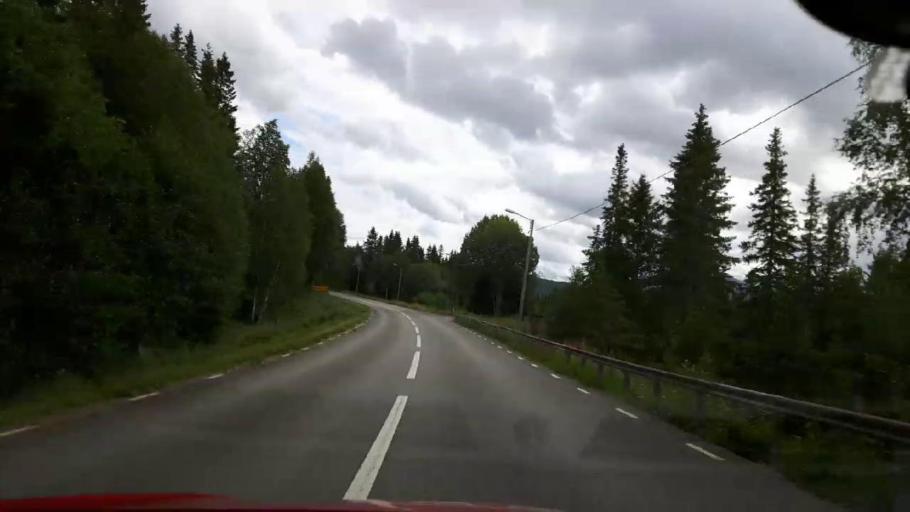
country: NO
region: Nord-Trondelag
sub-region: Lierne
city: Sandvika
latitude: 64.3910
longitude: 14.3741
